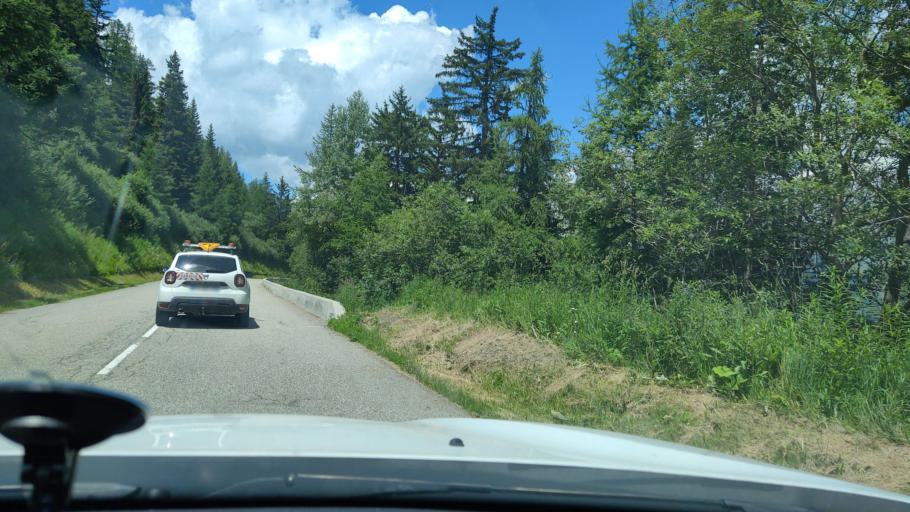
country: FR
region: Rhone-Alpes
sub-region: Departement de la Savoie
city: Seez
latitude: 45.5940
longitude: 6.8262
